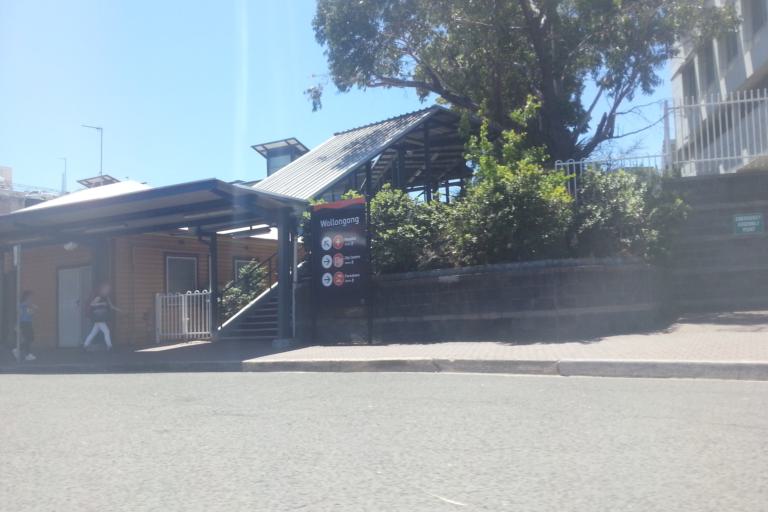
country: AU
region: New South Wales
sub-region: Wollongong
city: Wollongong
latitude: -34.4268
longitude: 150.8886
